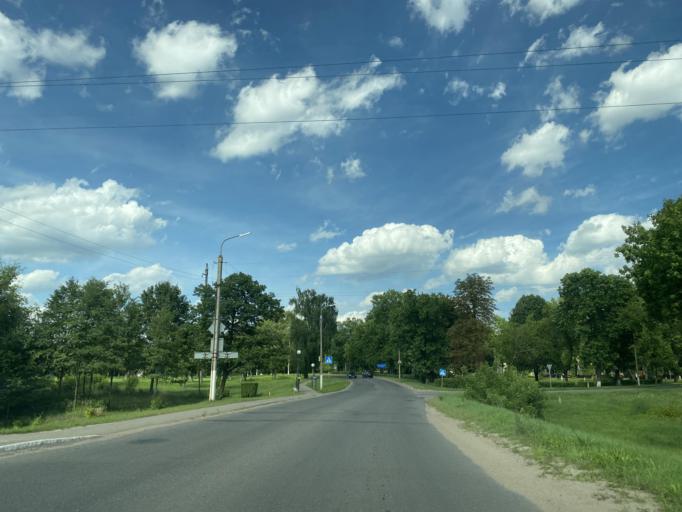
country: BY
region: Minsk
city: Horad Zhodzina
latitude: 54.0961
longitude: 28.3545
